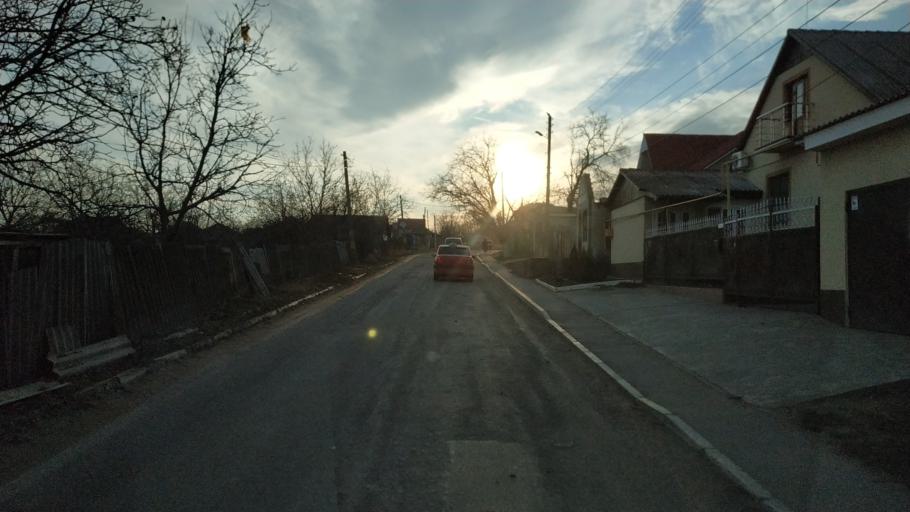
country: MD
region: Nisporeni
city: Nisporeni
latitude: 47.0872
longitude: 28.1743
